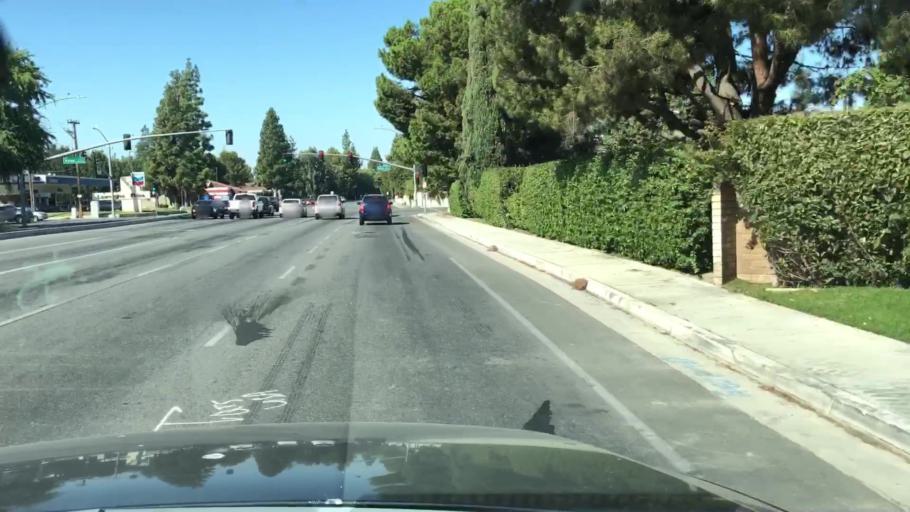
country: US
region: California
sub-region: Kern County
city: Greenacres
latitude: 35.3348
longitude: -119.0736
